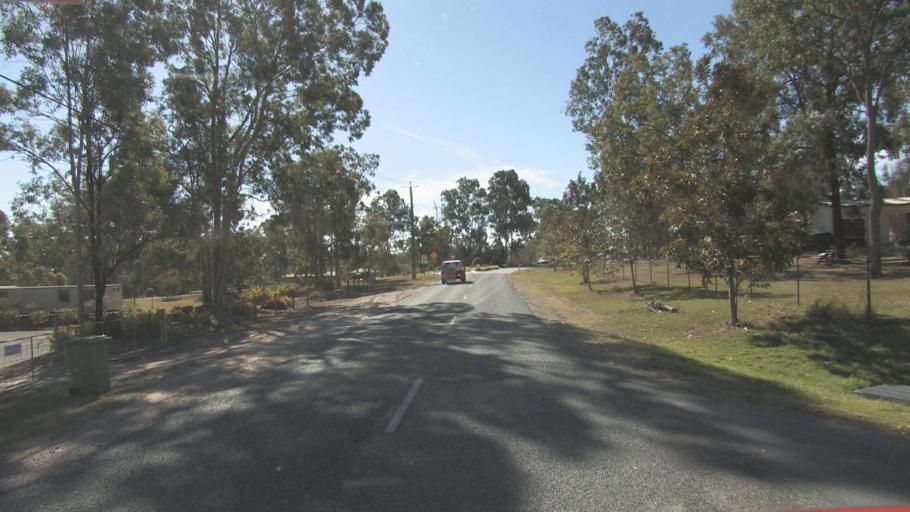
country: AU
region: Queensland
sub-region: Logan
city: North Maclean
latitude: -27.7364
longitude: 152.9600
